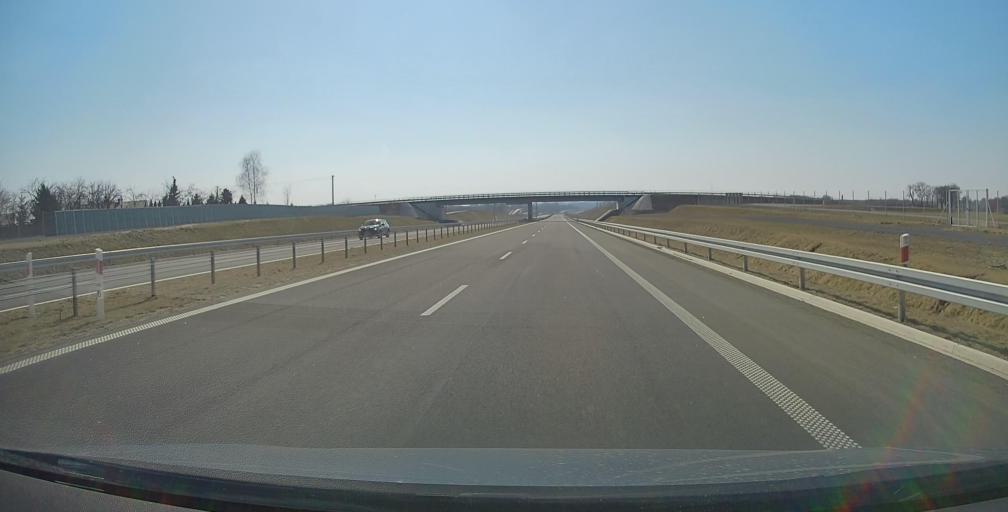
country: PL
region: Lublin Voivodeship
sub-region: Powiat krasnicki
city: Szastarka
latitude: 50.8273
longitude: 22.2985
